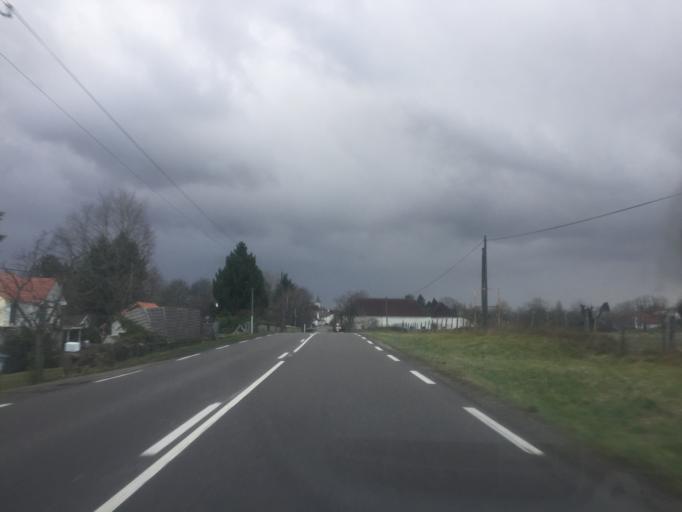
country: FR
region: Franche-Comte
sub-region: Departement du Jura
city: Dampierre
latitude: 47.1573
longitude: 5.7488
